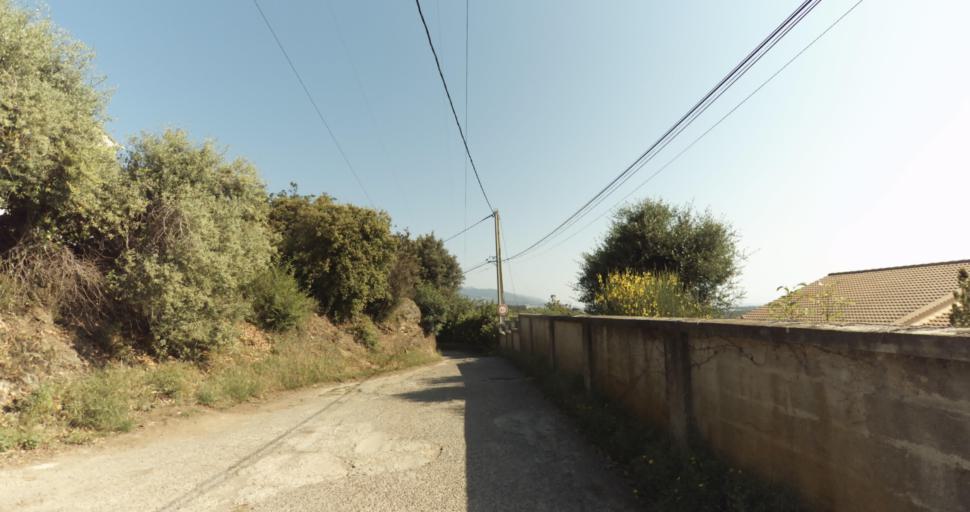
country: FR
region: Corsica
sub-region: Departement de la Haute-Corse
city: Biguglia
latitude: 42.6303
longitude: 9.4249
